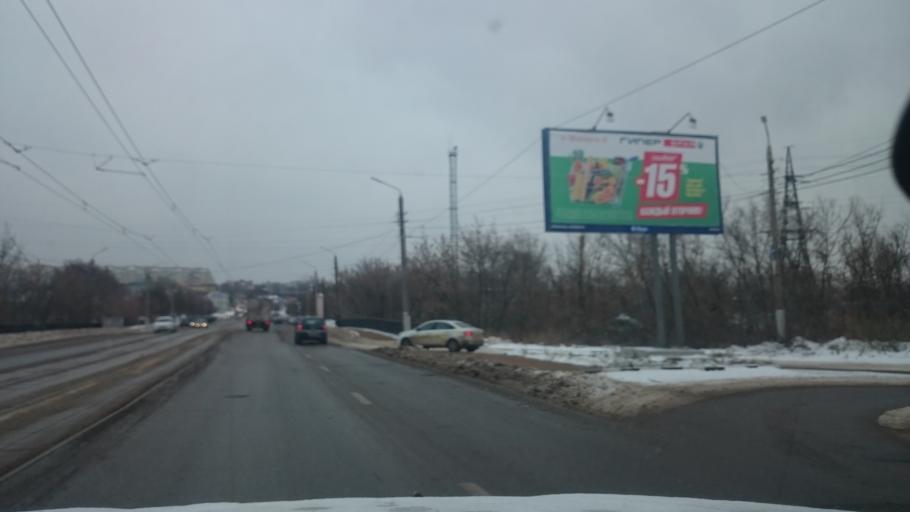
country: RU
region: Tula
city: Tula
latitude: 54.2026
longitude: 37.6250
